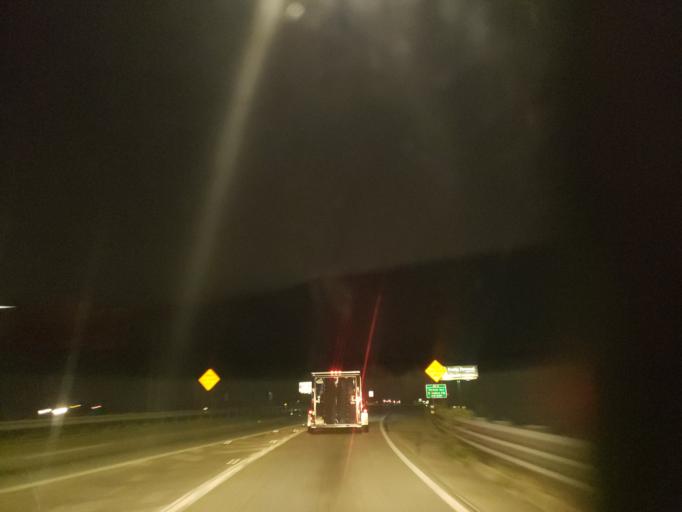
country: US
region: Georgia
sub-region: Chatham County
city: Savannah
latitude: 32.0687
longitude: -81.1363
